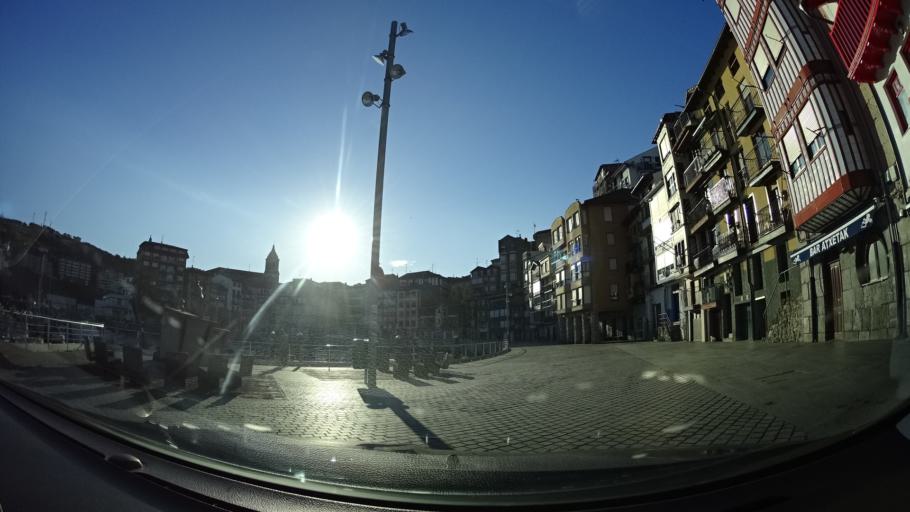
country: ES
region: Basque Country
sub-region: Bizkaia
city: Bermeo
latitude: 43.4207
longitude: -2.7197
